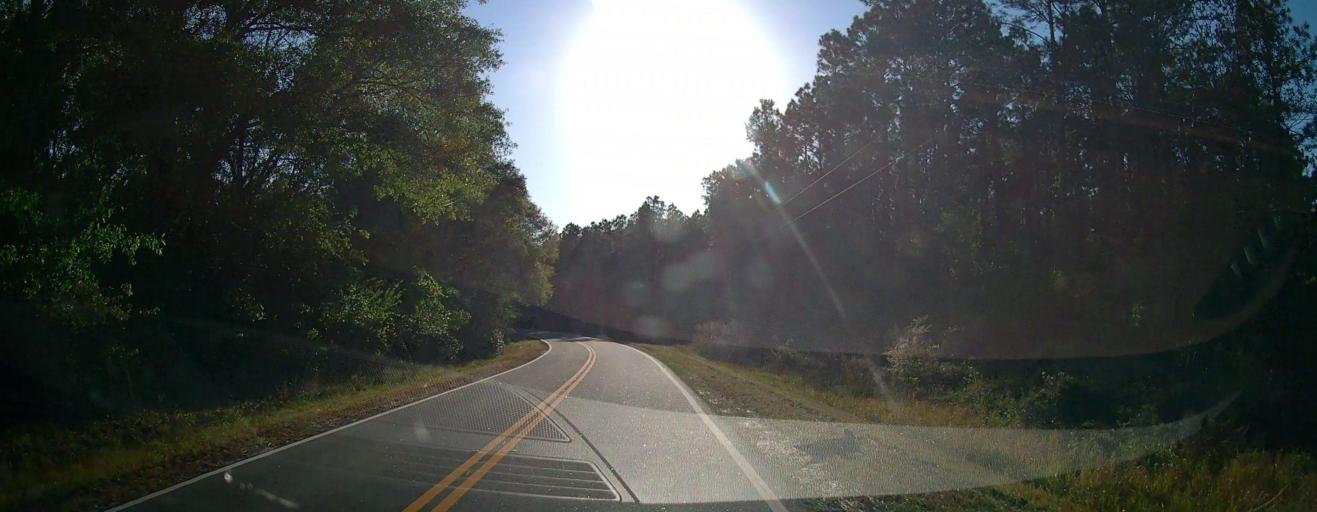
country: US
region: Georgia
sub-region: Ben Hill County
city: Fitzgerald
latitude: 31.6587
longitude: -83.1564
